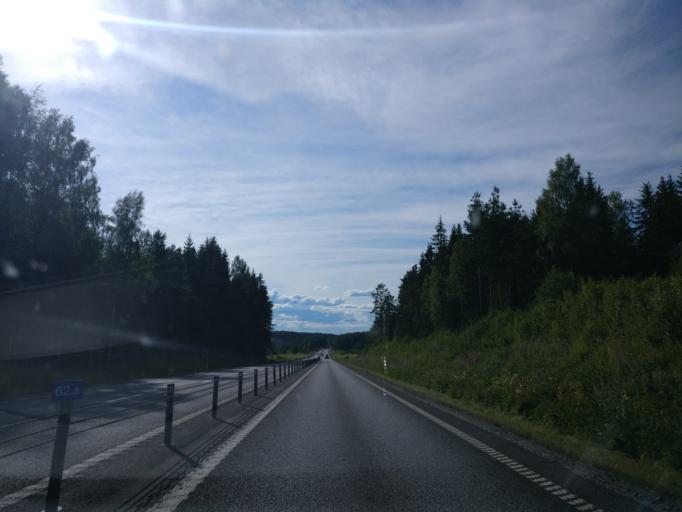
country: SE
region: Vaermland
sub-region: Arvika Kommun
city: Arvika
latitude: 59.6514
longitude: 12.6722
